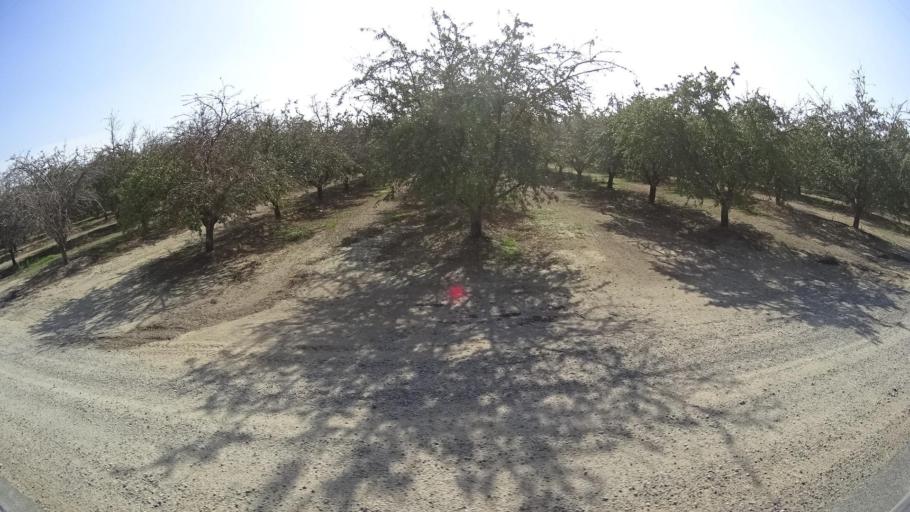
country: US
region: California
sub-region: Kern County
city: Shafter
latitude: 35.5296
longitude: -119.1754
